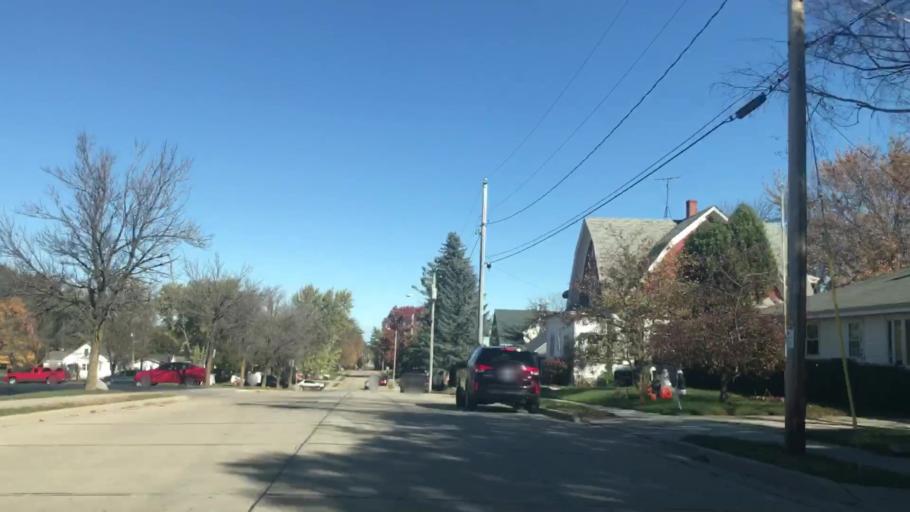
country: US
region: Wisconsin
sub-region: Dodge County
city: Mayville
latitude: 43.4943
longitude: -88.5524
